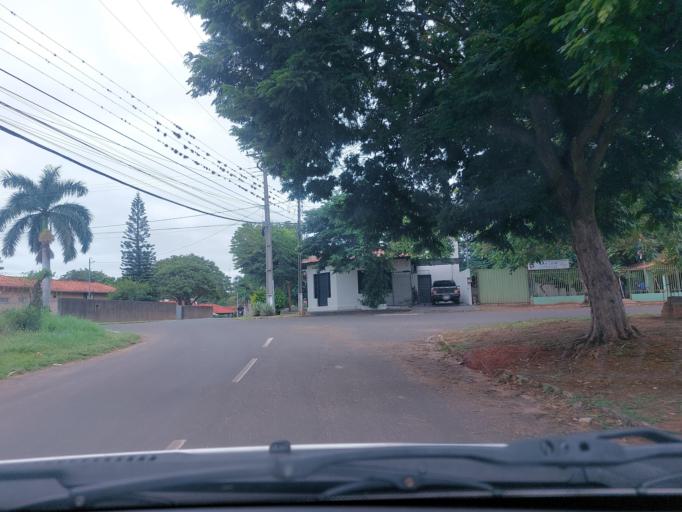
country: PY
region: San Pedro
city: Guayaybi
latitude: -24.6728
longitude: -56.4453
